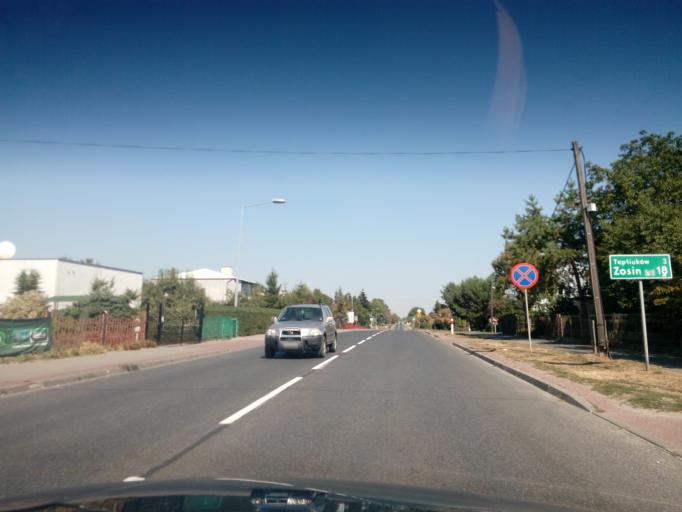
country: PL
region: Lublin Voivodeship
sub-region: Powiat hrubieszowski
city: Hrubieszow
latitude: 50.8050
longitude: 23.9057
